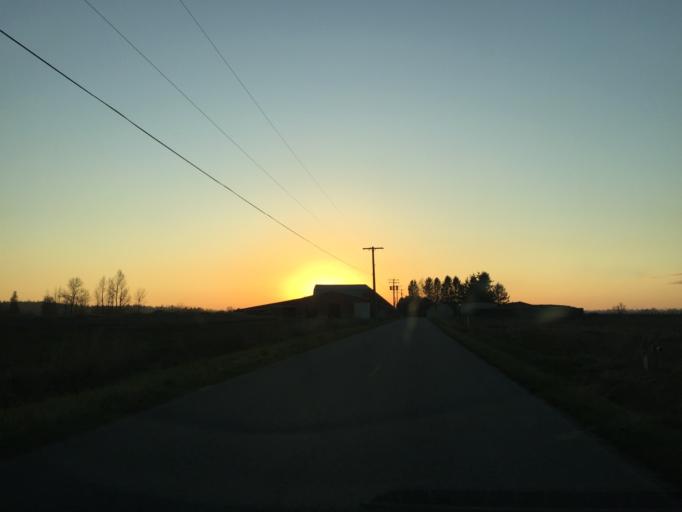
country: US
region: Washington
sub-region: Whatcom County
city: Sumas
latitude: 48.9827
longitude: -122.2129
